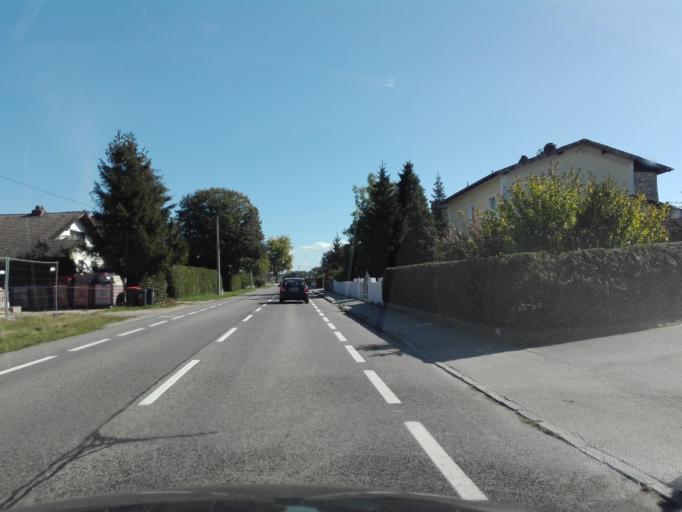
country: AT
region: Lower Austria
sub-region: Politischer Bezirk Amstetten
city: Ennsdorf
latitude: 48.2106
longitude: 14.4933
